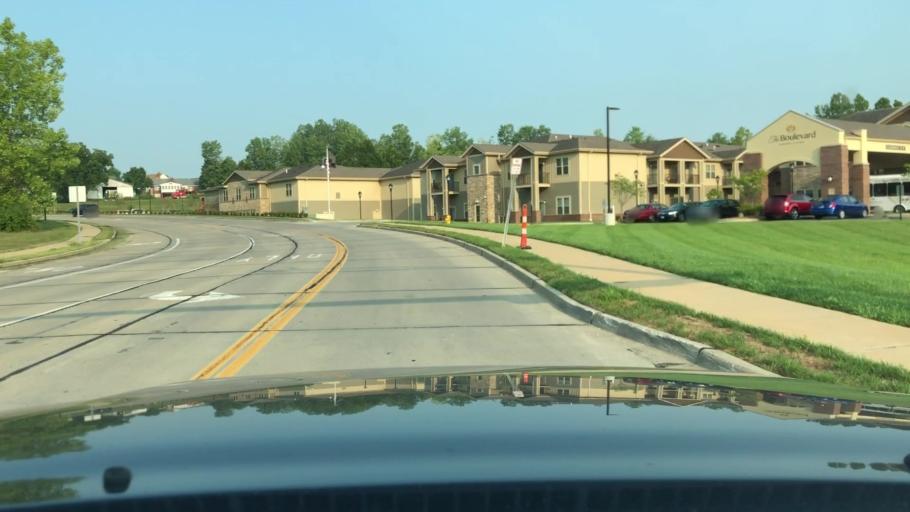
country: US
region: Missouri
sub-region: Saint Charles County
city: Saint Peters
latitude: 38.8055
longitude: -90.5532
